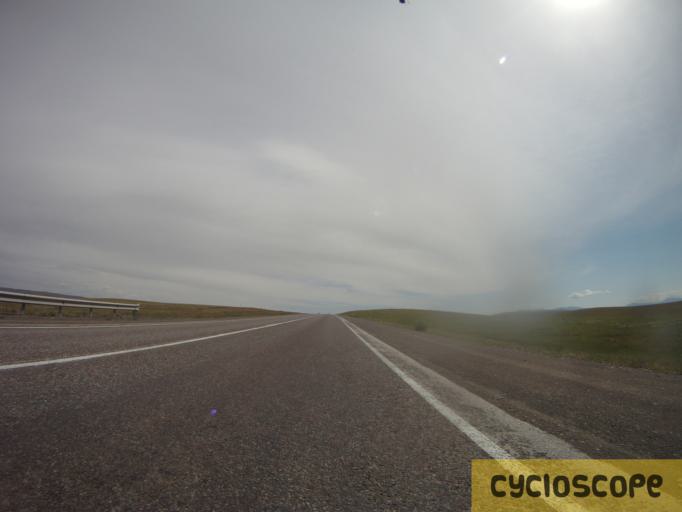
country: KZ
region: Zhambyl
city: Georgiyevka
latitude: 43.2753
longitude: 74.8444
